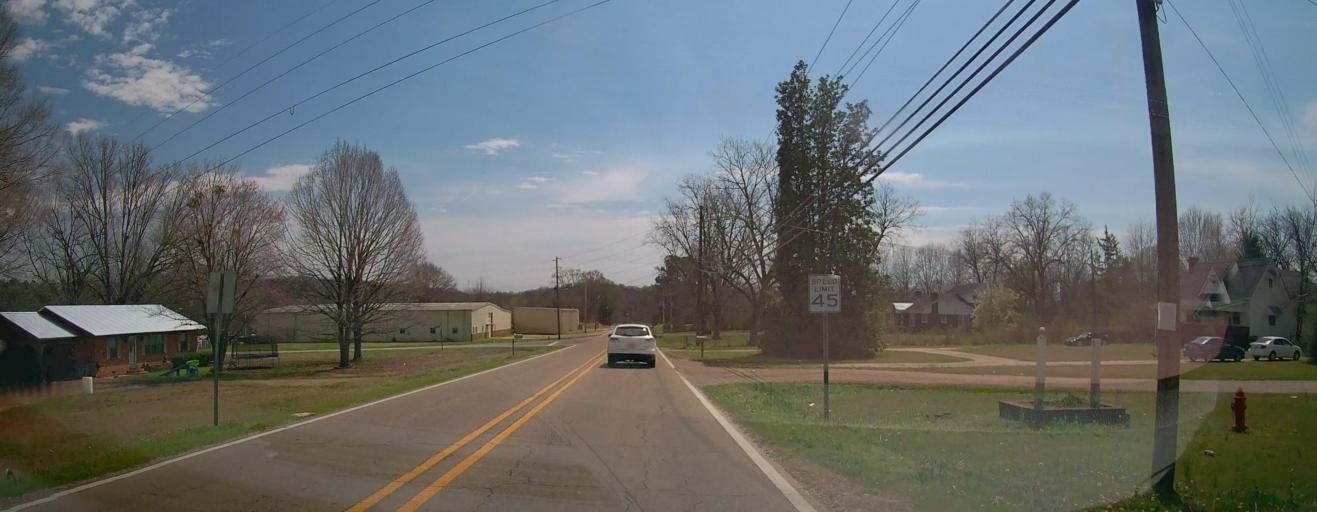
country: US
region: Mississippi
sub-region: Union County
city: New Albany
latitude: 34.4747
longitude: -88.9948
